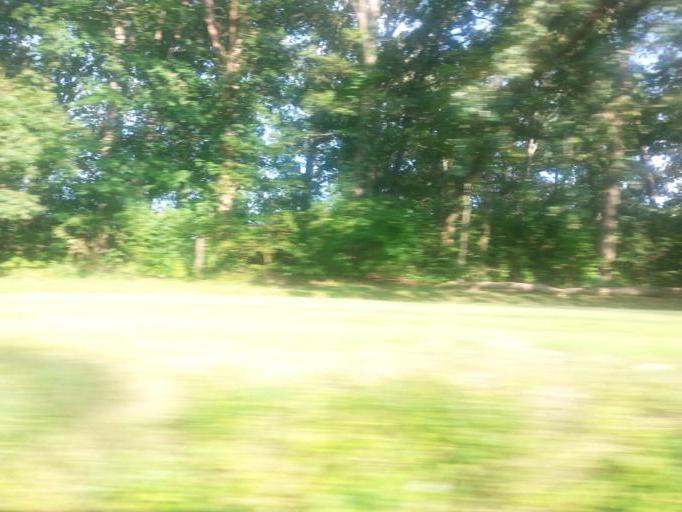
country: US
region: Tennessee
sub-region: Sevier County
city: Seymour
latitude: 35.8499
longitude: -83.7855
